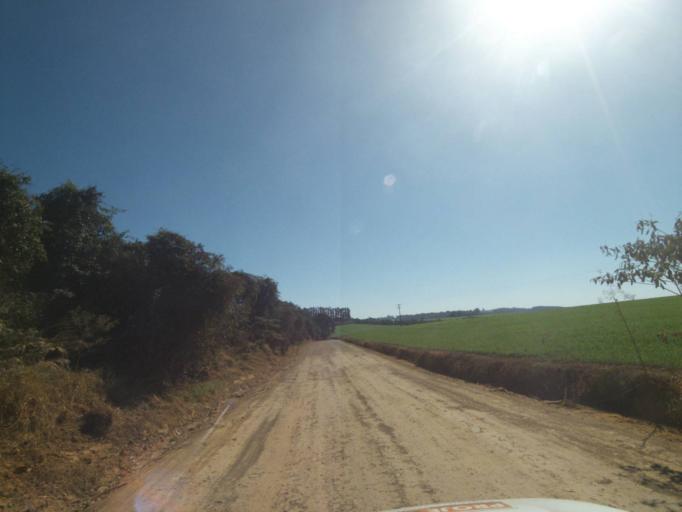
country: BR
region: Parana
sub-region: Reserva
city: Reserva
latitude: -24.6270
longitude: -50.6266
